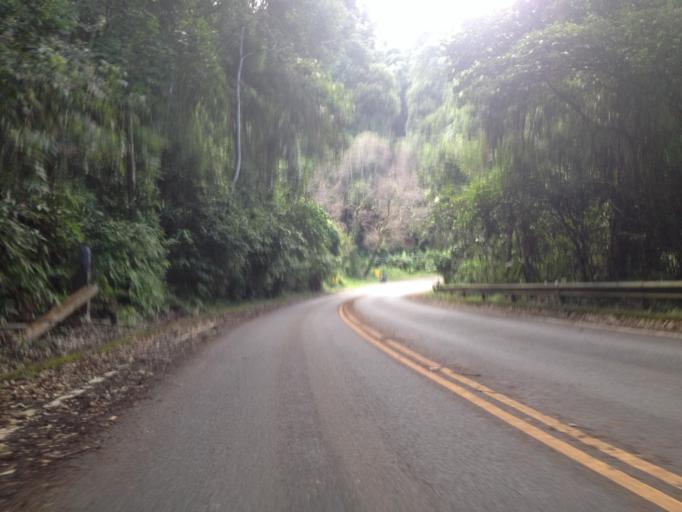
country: TH
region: Chiang Mai
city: Chiang Mai
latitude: 18.8045
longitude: 98.9100
